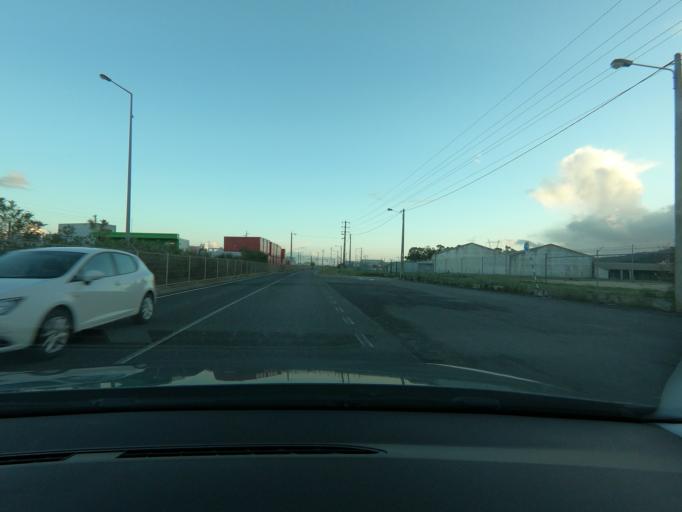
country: PT
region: Lisbon
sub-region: Vila Franca de Xira
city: Castanheira do Ribatejo
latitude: 38.9942
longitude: -8.9631
